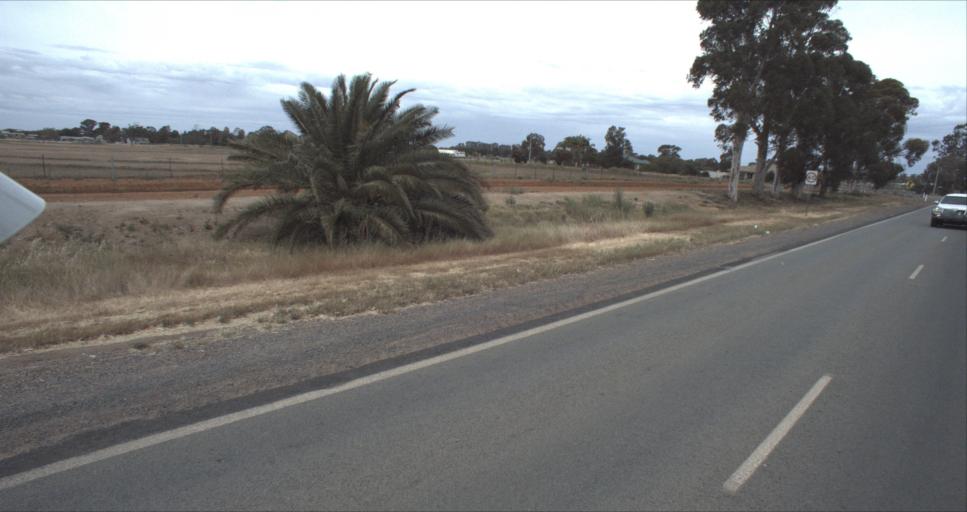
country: AU
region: New South Wales
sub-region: Leeton
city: Leeton
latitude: -34.5329
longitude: 146.4092
